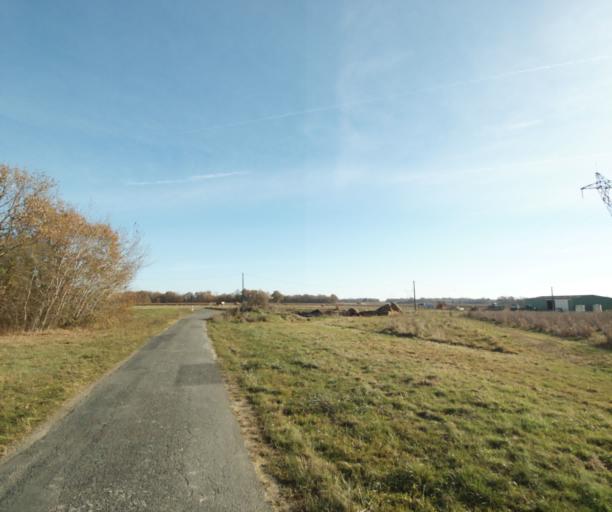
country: FR
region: Poitou-Charentes
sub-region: Departement de la Charente-Maritime
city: Cherac
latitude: 45.7446
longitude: -0.4824
